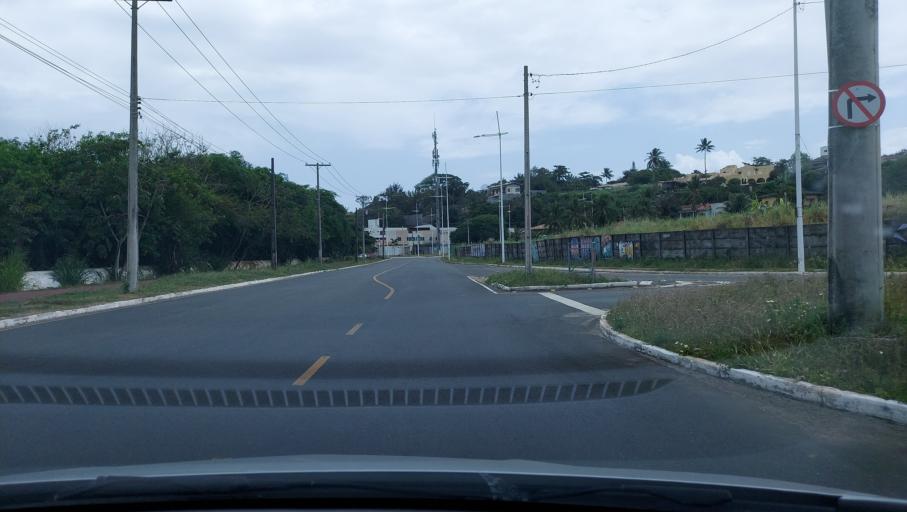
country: BR
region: Bahia
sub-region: Lauro De Freitas
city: Lauro de Freitas
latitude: -12.9519
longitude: -38.3935
